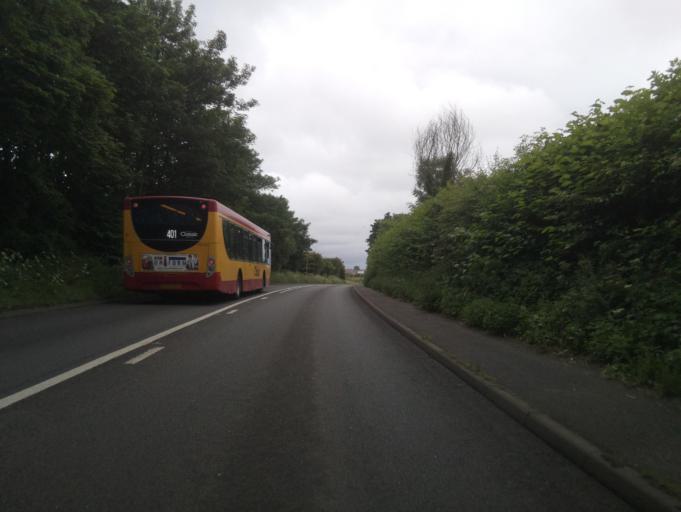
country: GB
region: England
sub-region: Staffordshire
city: Burton upon Trent
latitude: 52.8436
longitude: -1.6739
